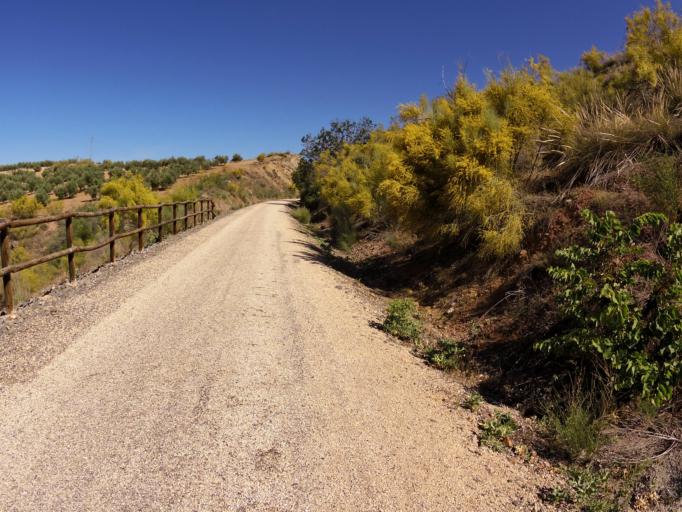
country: ES
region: Andalusia
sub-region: Provincia de Jaen
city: Alcaudete
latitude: 37.6007
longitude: -4.1578
